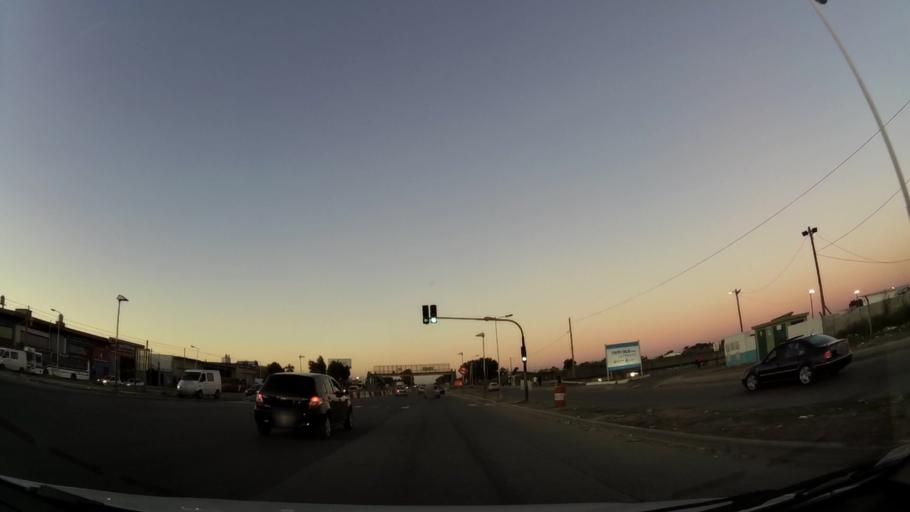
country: AR
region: Buenos Aires
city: San Justo
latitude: -34.7286
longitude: -58.6006
